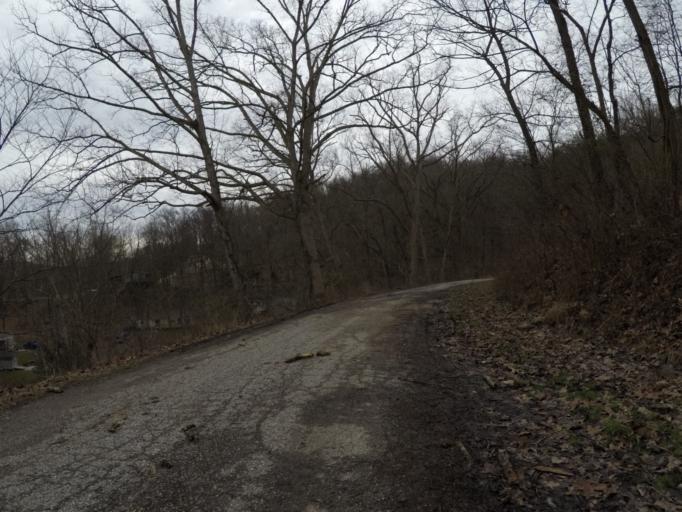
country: US
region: Ohio
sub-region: Lawrence County
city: Burlington
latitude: 38.3916
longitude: -82.5181
